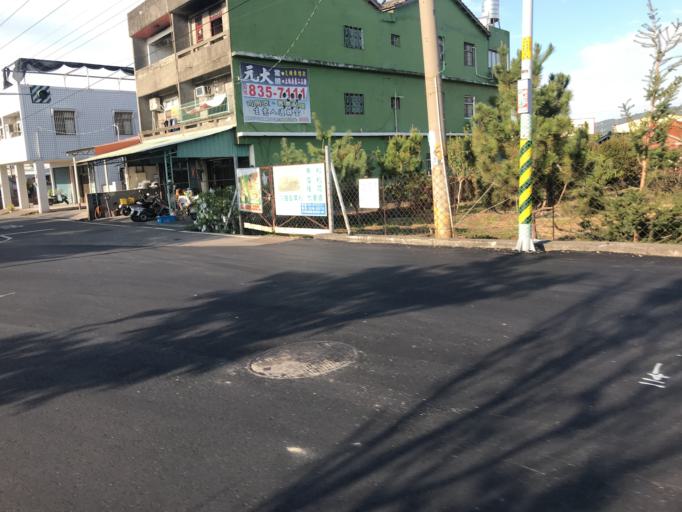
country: TW
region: Taiwan
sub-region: Nantou
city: Nantou
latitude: 23.8958
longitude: 120.5989
